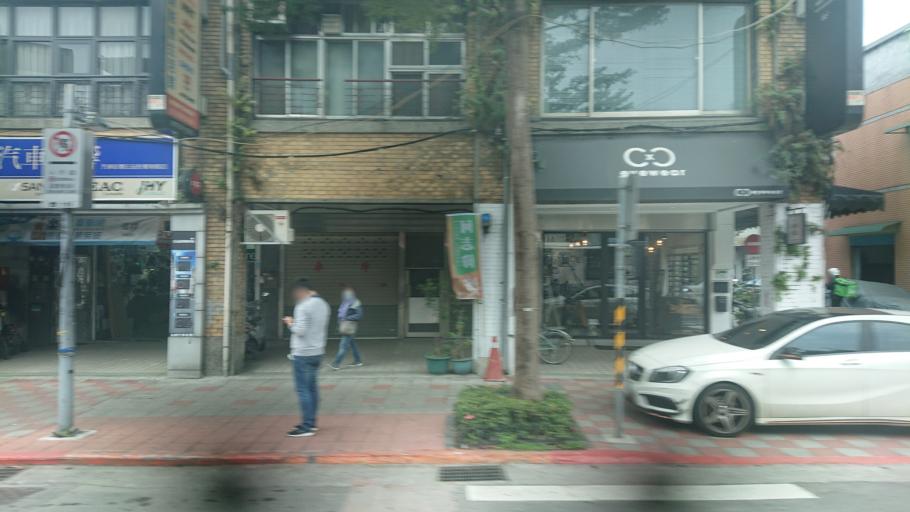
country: TW
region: Taipei
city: Taipei
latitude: 25.0720
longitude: 121.5173
